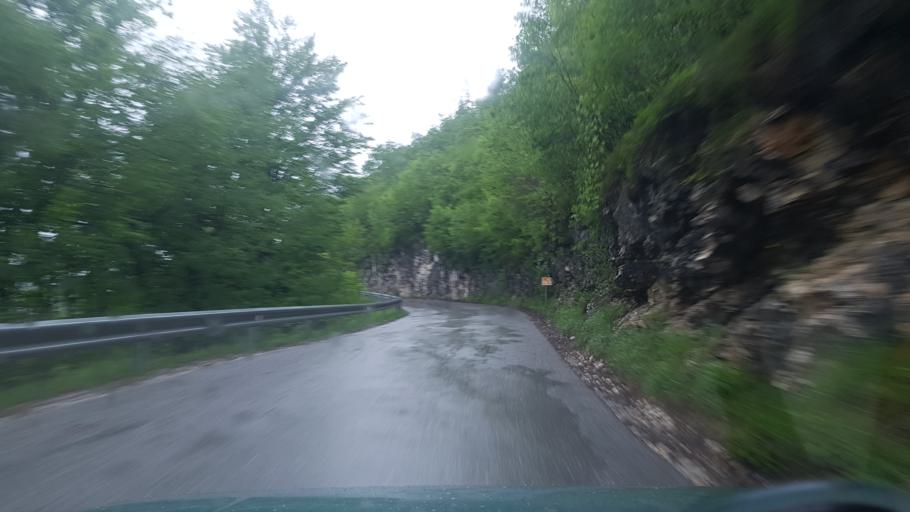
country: SI
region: Bohinj
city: Bohinjska Bistrica
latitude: 46.2736
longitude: 14.0051
